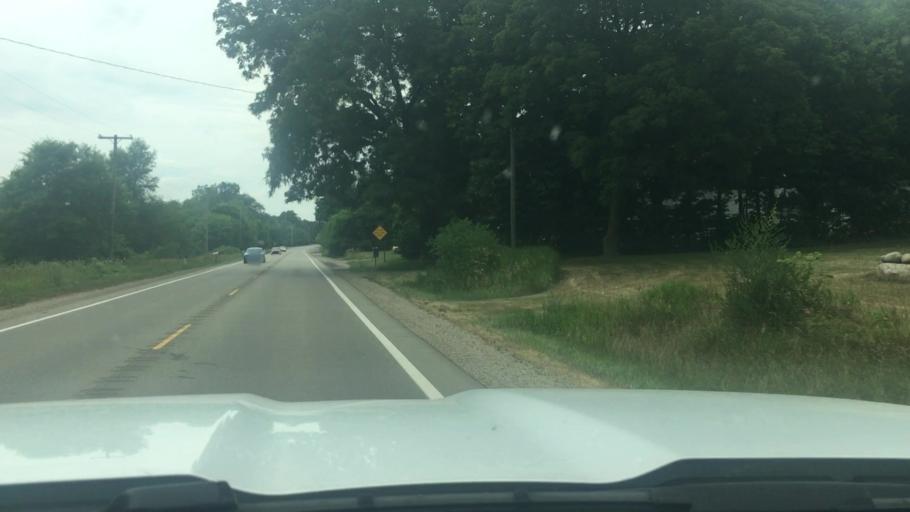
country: US
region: Michigan
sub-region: Kent County
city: Lowell
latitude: 42.9372
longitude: -85.3179
